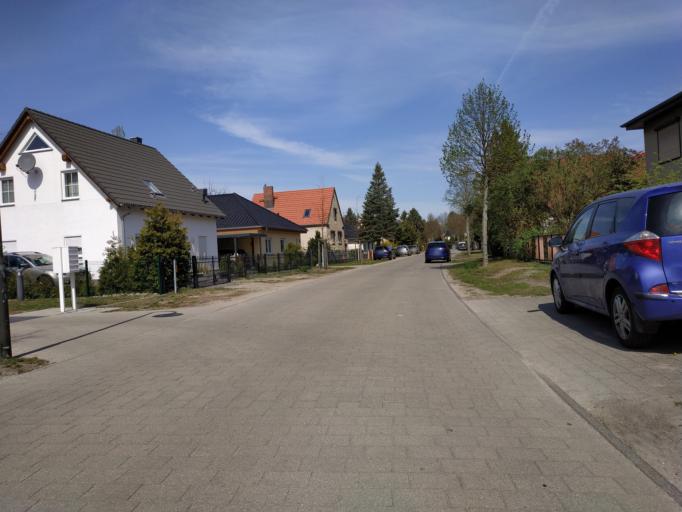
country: DE
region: Brandenburg
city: Petershagen
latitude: 52.5404
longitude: 13.8204
